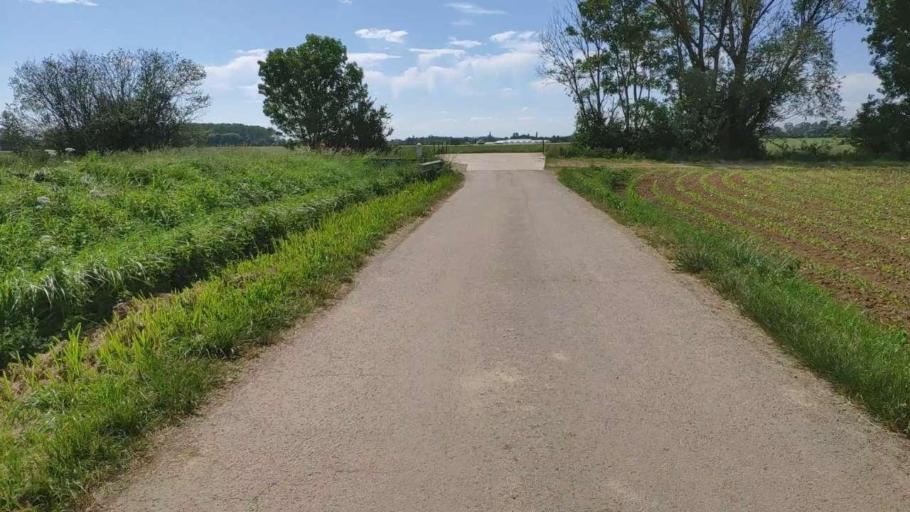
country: FR
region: Franche-Comte
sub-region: Departement du Jura
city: Bletterans
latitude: 46.7314
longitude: 5.4914
